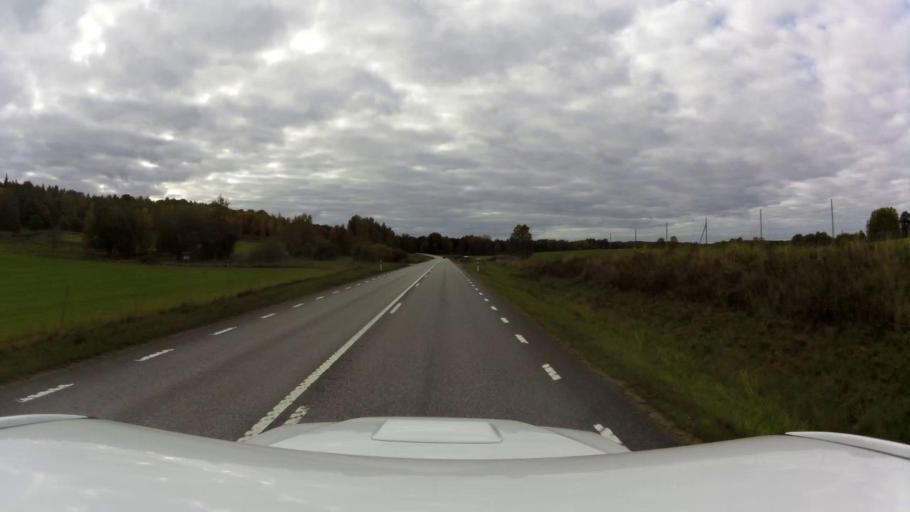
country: SE
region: OEstergoetland
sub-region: Kinda Kommun
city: Rimforsa
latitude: 58.1926
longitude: 15.6668
